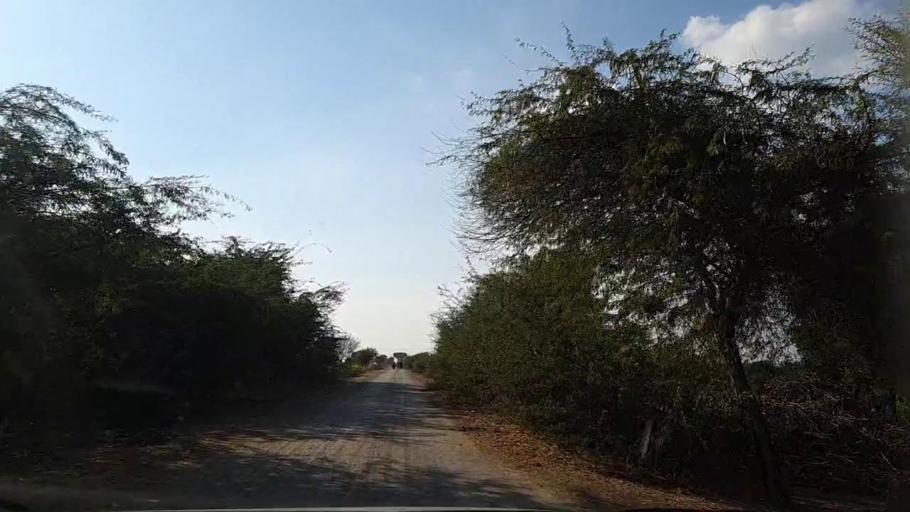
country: PK
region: Sindh
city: Pithoro
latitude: 25.6511
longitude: 69.2670
